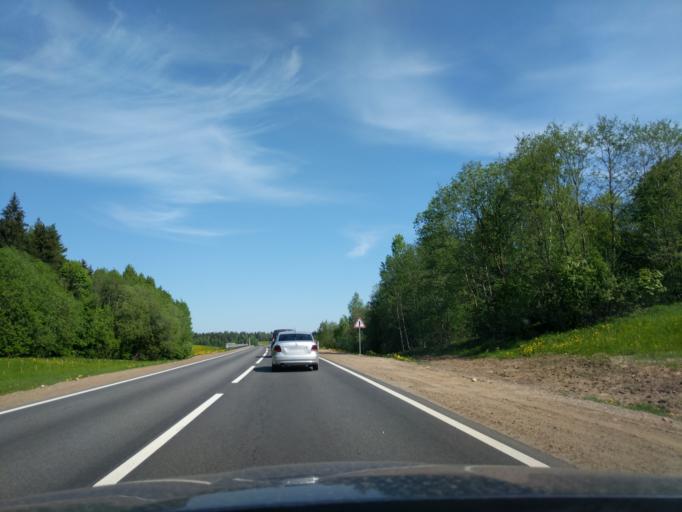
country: BY
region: Minsk
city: Bal'shavik
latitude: 54.0957
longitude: 27.5354
